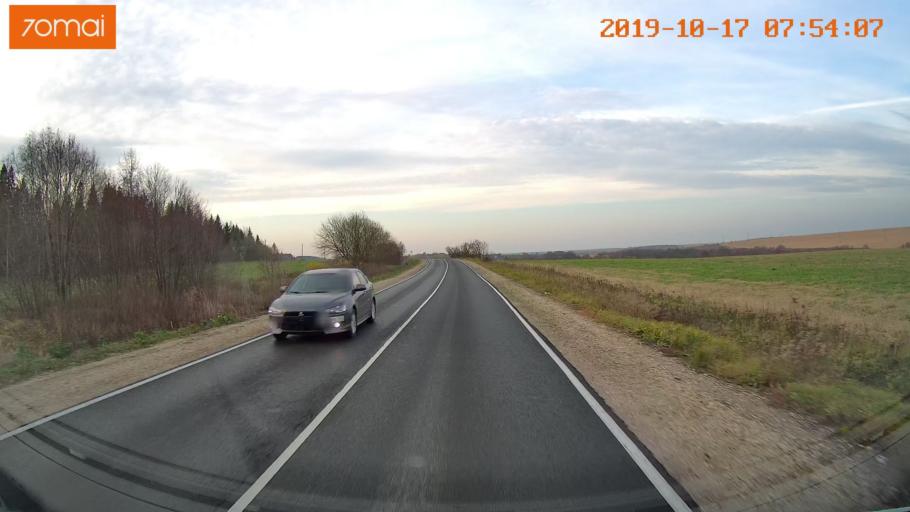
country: RU
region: Vladimir
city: Bavleny
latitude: 56.4541
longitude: 39.6097
